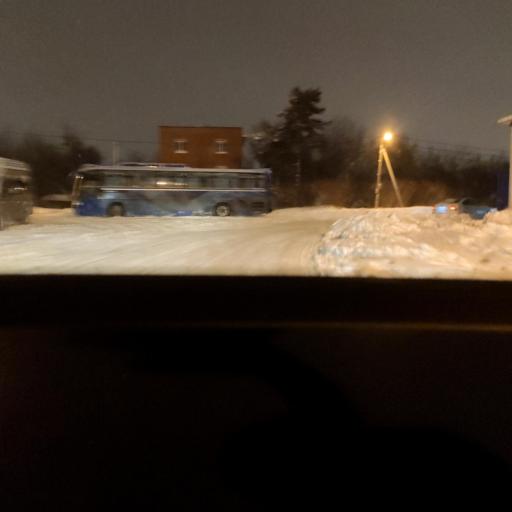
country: RU
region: Moskovskaya
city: Odintsovo
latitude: 55.6657
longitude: 37.2645
